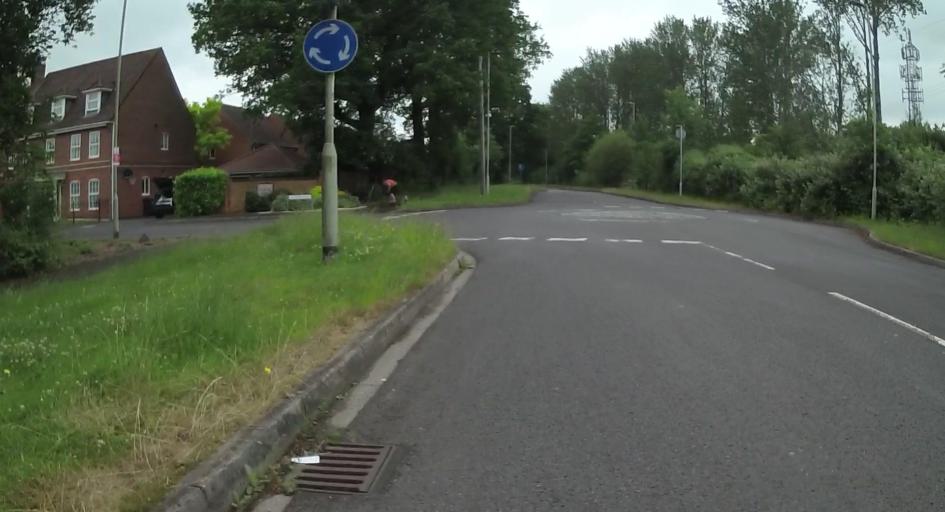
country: GB
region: England
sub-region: West Berkshire
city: Arborfield
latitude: 51.3872
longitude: -0.9044
